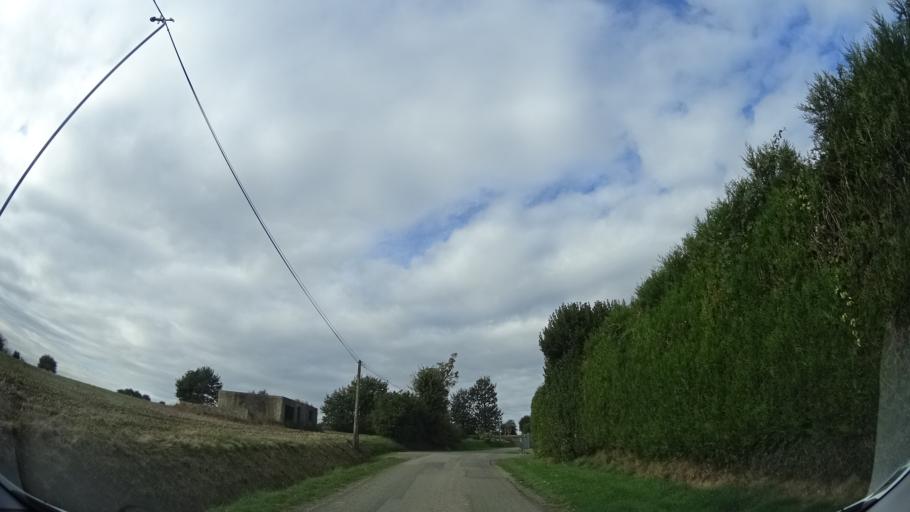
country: FR
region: Brittany
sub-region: Departement d'Ille-et-Vilaine
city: Vignoc
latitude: 48.2393
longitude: -1.7916
